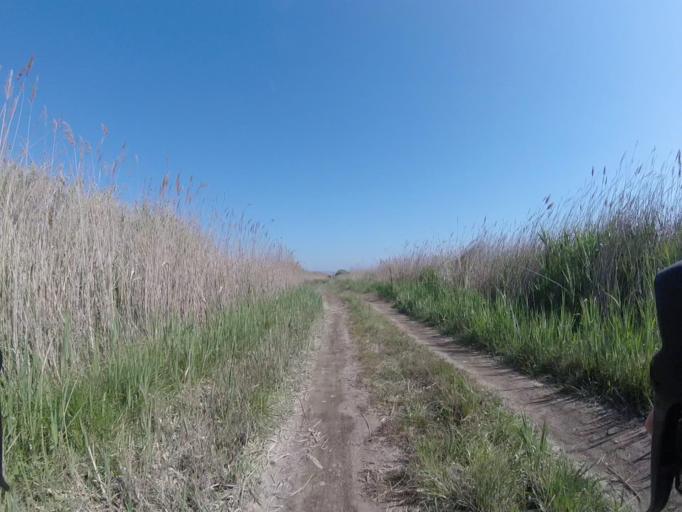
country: ES
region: Valencia
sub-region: Provincia de Castello
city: Torreblanca
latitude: 40.1658
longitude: 0.1727
